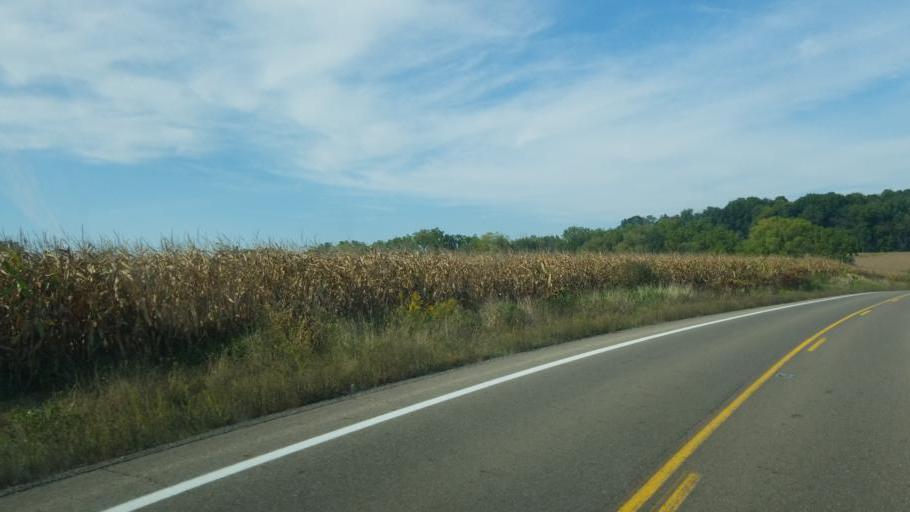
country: US
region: Ohio
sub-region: Knox County
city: Gambier
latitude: 40.3075
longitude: -82.3289
